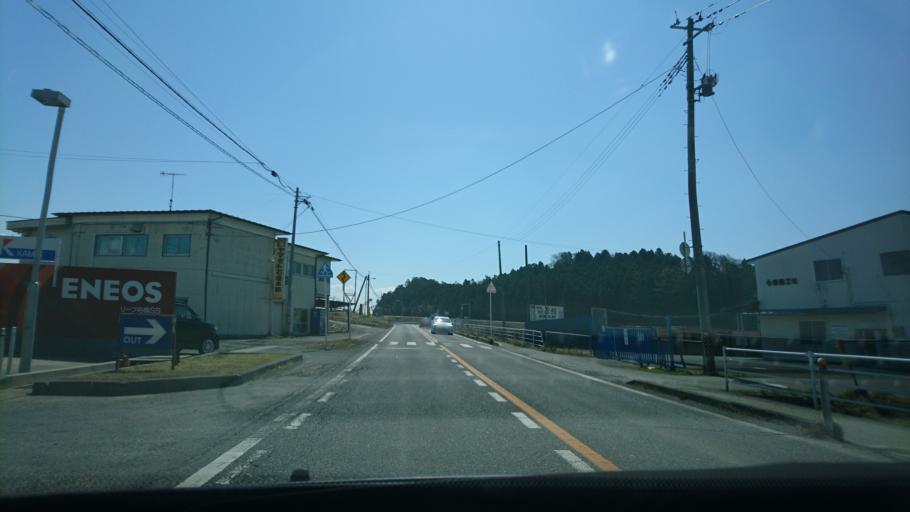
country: JP
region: Miyagi
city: Wakuya
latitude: 38.7036
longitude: 141.1859
